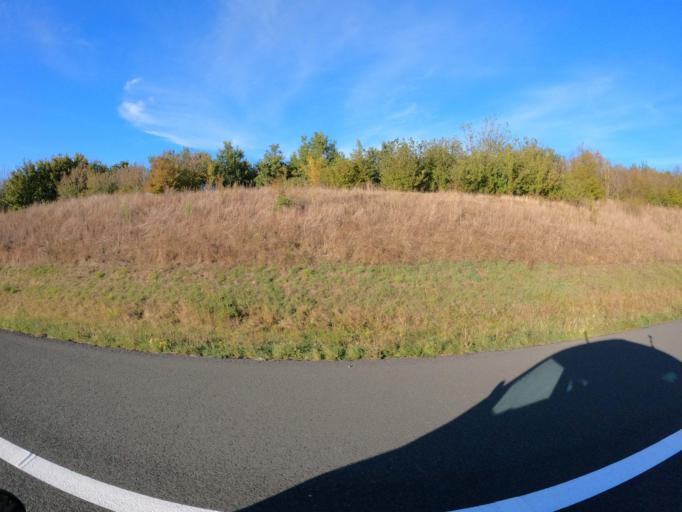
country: FR
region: Pays de la Loire
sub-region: Departement de Maine-et-Loire
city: Saint-Lambert-du-Lattay
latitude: 47.2420
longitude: -0.6557
